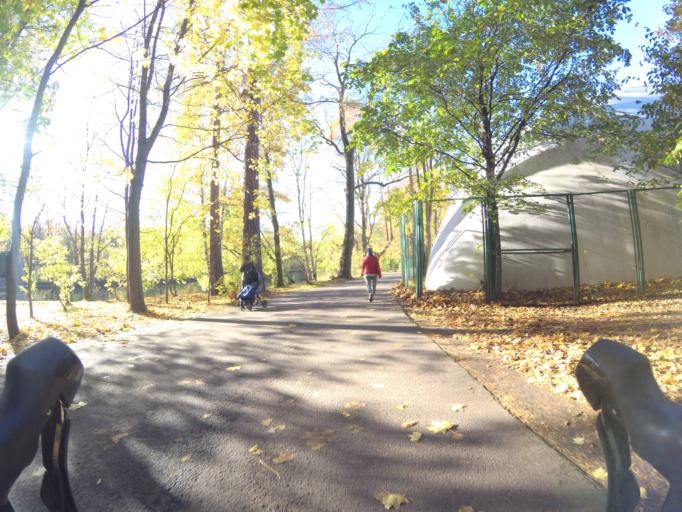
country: RU
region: Leningrad
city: Krestovskiy ostrov
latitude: 59.9817
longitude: 30.2621
